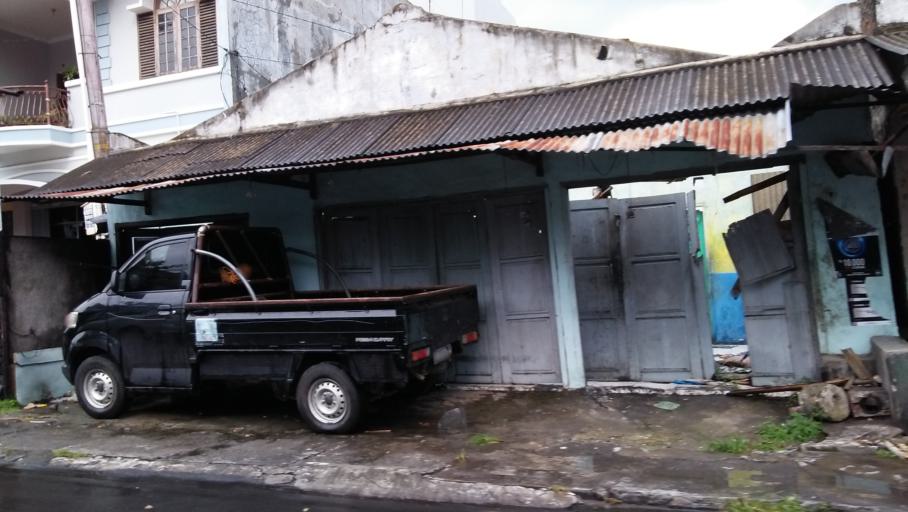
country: ID
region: Daerah Istimewa Yogyakarta
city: Depok
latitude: -7.7795
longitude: 110.4001
